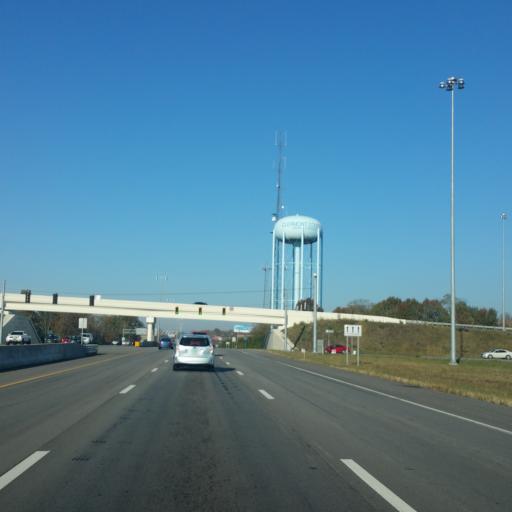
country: US
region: Ohio
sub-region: Clermont County
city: Summerside
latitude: 39.1020
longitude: -84.2851
